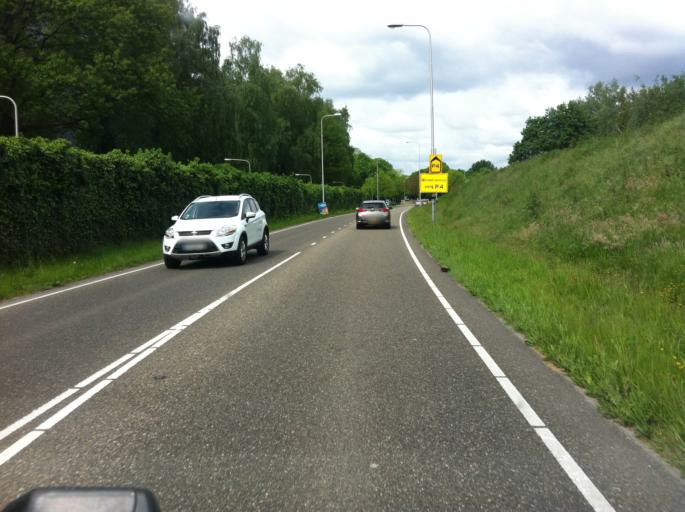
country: NL
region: Limburg
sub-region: Gemeente Roerdalen
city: Melick
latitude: 51.1839
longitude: 6.0129
